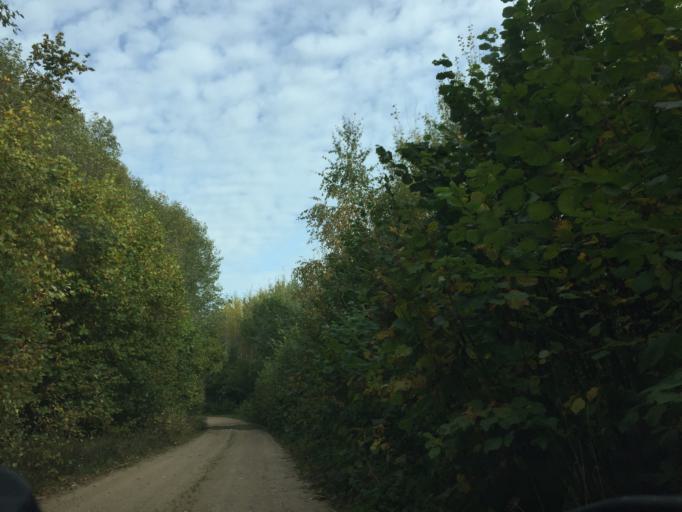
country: LV
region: Jaunpils
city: Jaunpils
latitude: 56.6452
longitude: 23.0783
